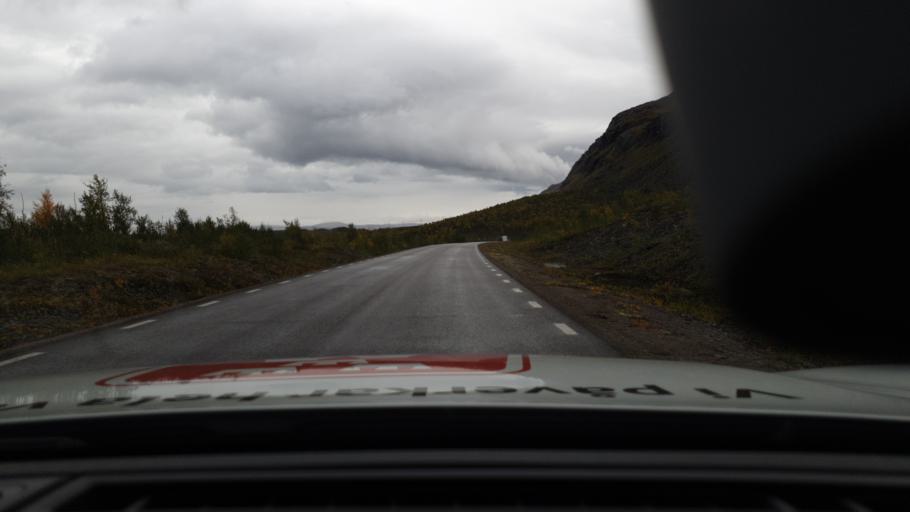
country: NO
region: Troms
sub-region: Bardu
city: Setermoen
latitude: 68.4266
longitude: 18.3709
